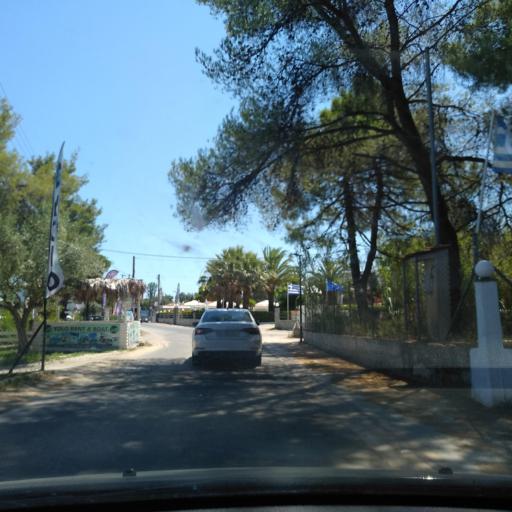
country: GR
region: Central Macedonia
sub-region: Nomos Chalkidikis
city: Neos Marmaras
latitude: 40.1869
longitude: 23.7906
